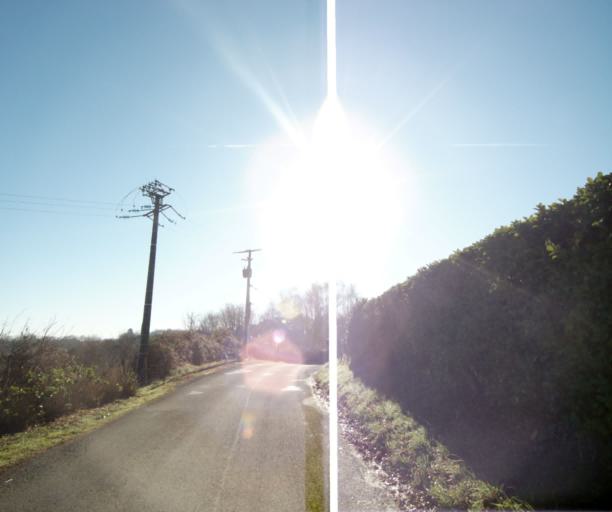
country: FR
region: Aquitaine
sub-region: Departement des Pyrenees-Atlantiques
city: Ciboure
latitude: 43.3665
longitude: -1.6626
